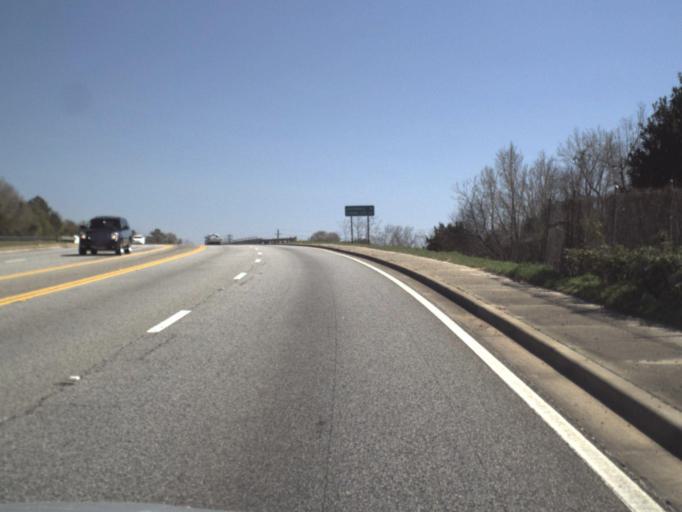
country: US
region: Florida
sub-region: Jackson County
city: Graceville
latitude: 30.9465
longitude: -85.4002
